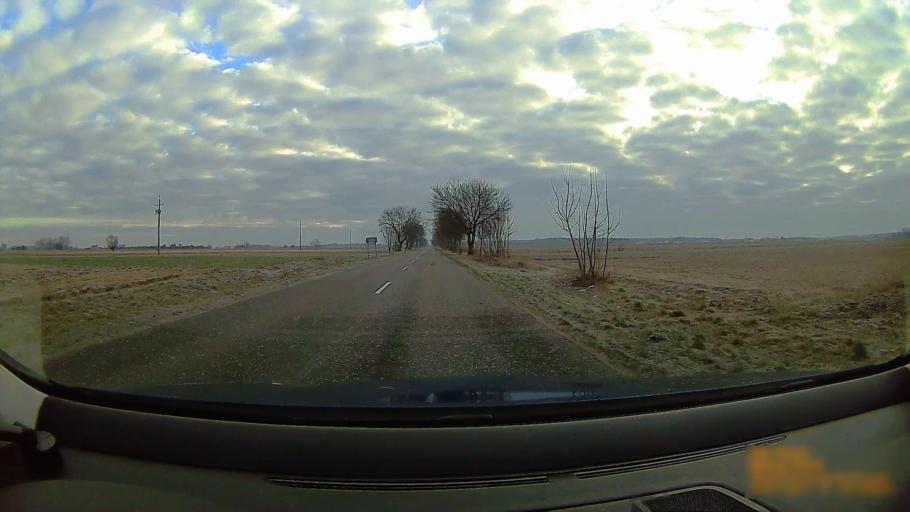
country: PL
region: Greater Poland Voivodeship
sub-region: Powiat koninski
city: Stare Miasto
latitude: 52.2000
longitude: 18.1791
